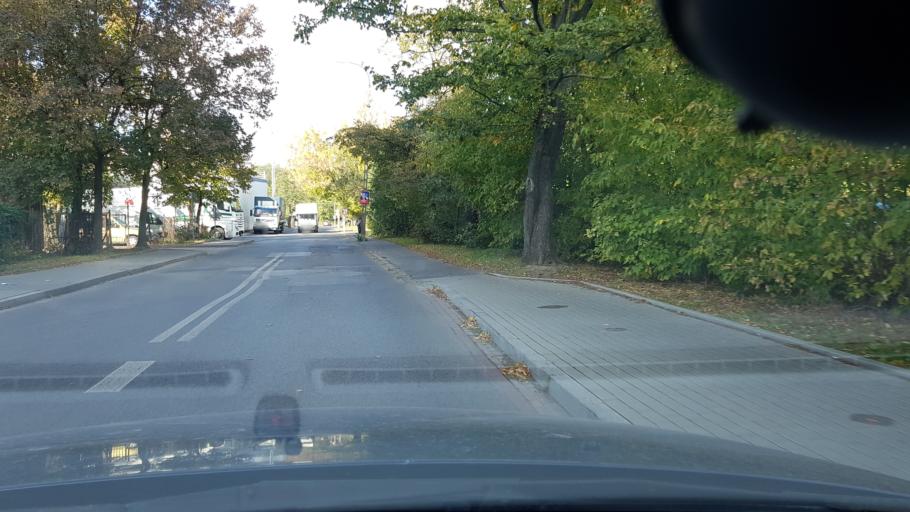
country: PL
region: Masovian Voivodeship
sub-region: Warszawa
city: Bielany
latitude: 52.2771
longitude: 20.9309
